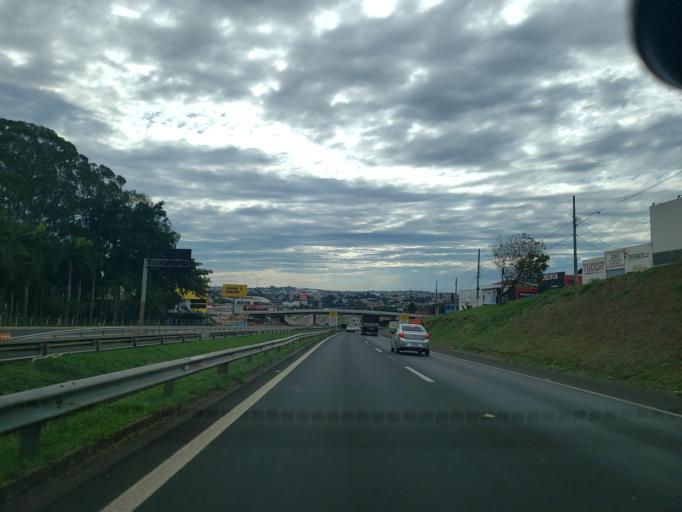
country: BR
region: Sao Paulo
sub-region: Bauru
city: Bauru
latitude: -22.3212
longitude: -49.0532
